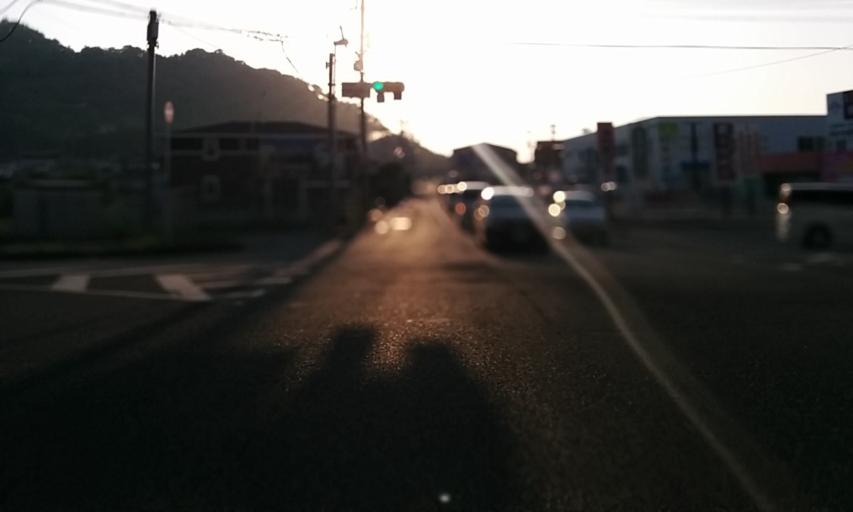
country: JP
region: Ehime
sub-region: Shikoku-chuo Shi
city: Matsuyama
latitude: 33.7820
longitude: 132.7875
